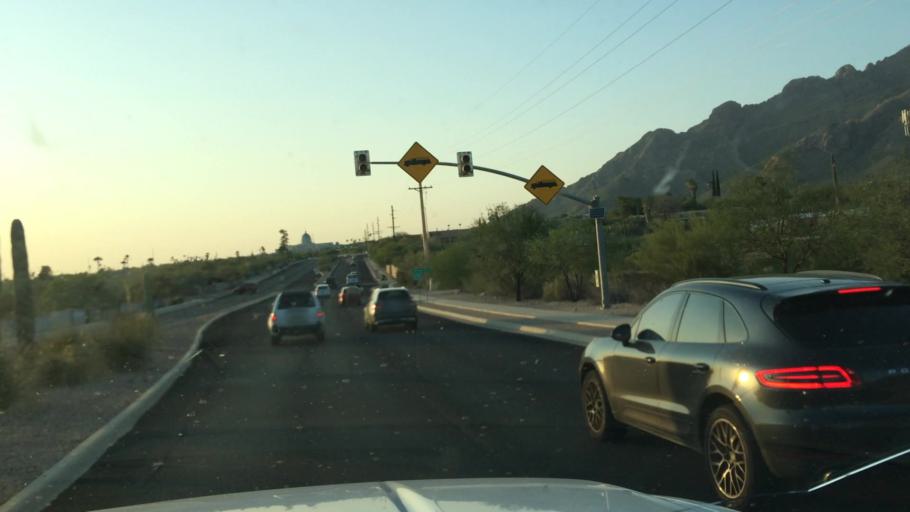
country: US
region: Arizona
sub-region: Pima County
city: Catalina Foothills
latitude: 32.3317
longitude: -110.9441
